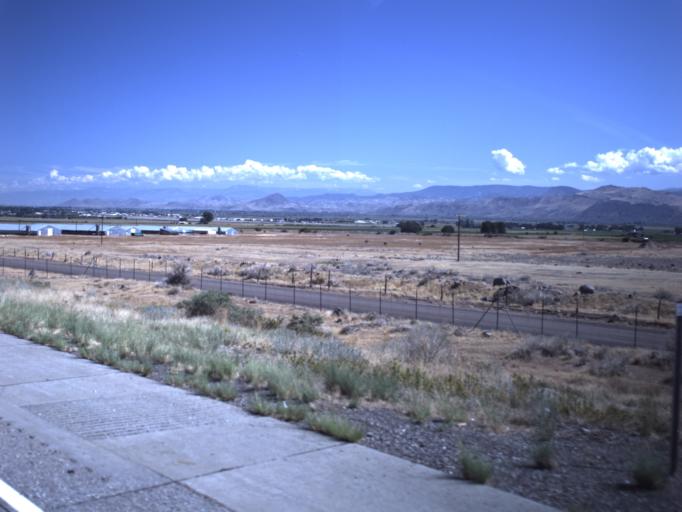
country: US
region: Utah
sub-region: Sevier County
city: Richfield
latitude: 38.7135
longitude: -112.1356
